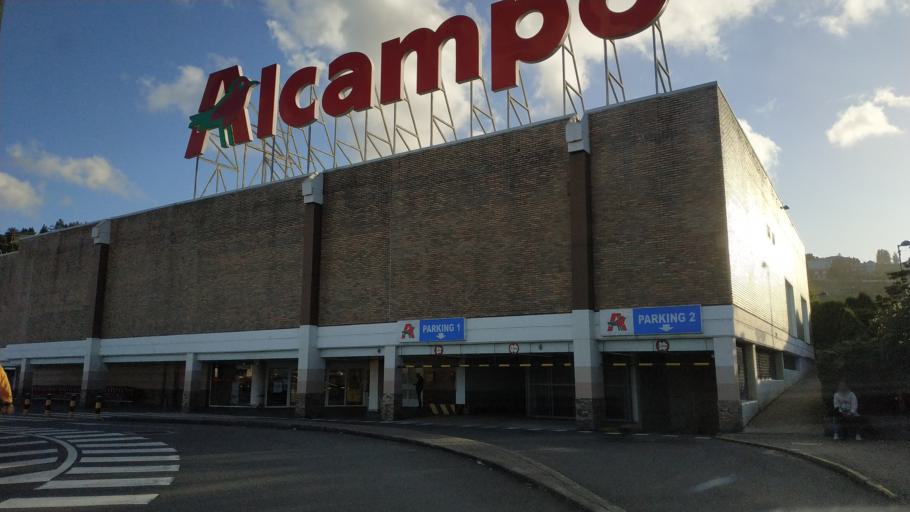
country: ES
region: Galicia
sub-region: Provincia da Coruna
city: Culleredo
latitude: 43.3295
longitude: -8.3910
